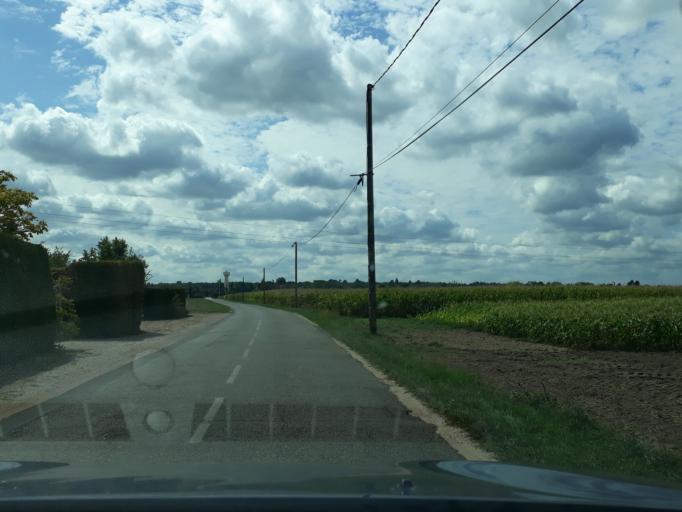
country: FR
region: Centre
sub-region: Departement du Loiret
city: Saint-Cyr-en-Val
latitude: 47.8430
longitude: 1.9716
